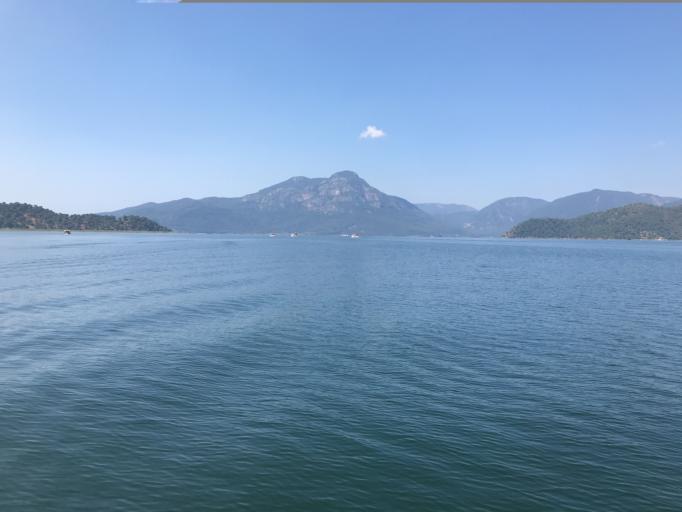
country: TR
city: Dalyan
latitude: 36.9115
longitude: 28.6537
